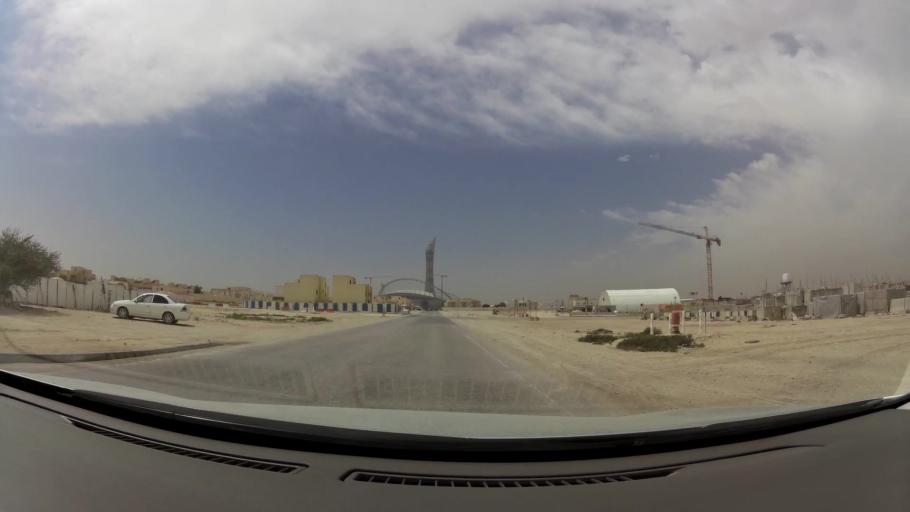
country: QA
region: Baladiyat ar Rayyan
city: Ar Rayyan
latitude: 25.2689
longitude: 51.4605
